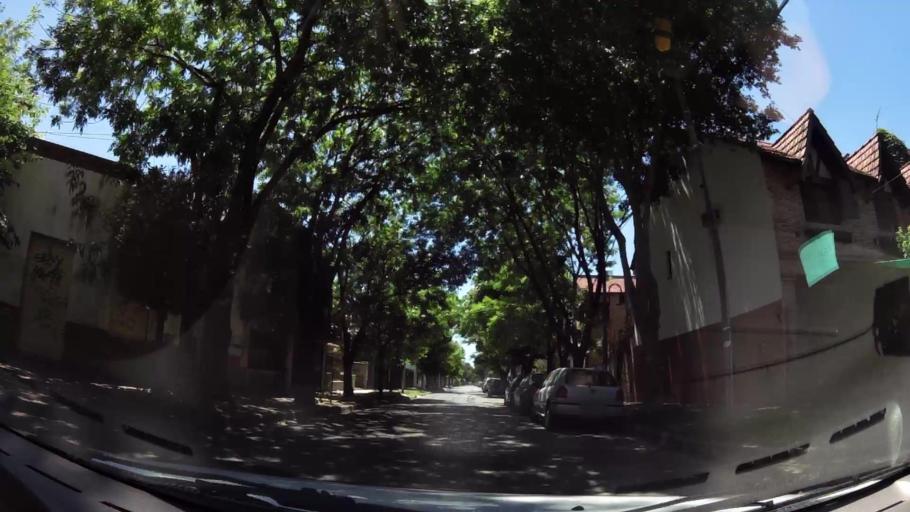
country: AR
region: Buenos Aires
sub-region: Partido de Vicente Lopez
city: Olivos
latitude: -34.5048
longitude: -58.5003
